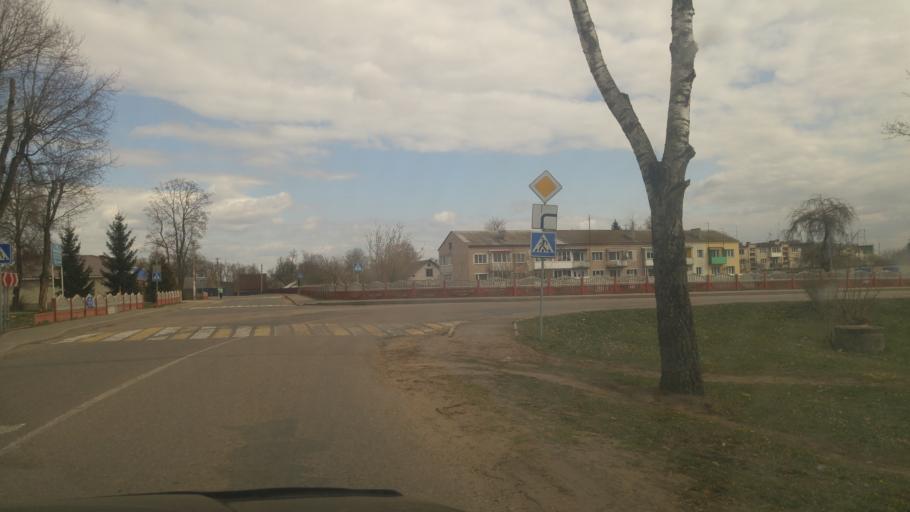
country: BY
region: Minsk
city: Rudzyensk
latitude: 53.6584
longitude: 27.8019
